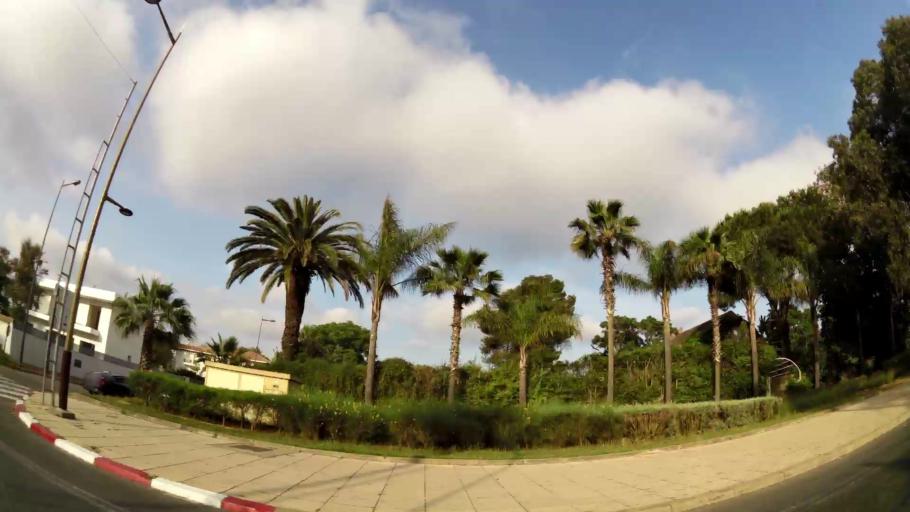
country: MA
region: Rabat-Sale-Zemmour-Zaer
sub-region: Rabat
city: Rabat
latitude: 33.9572
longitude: -6.8255
